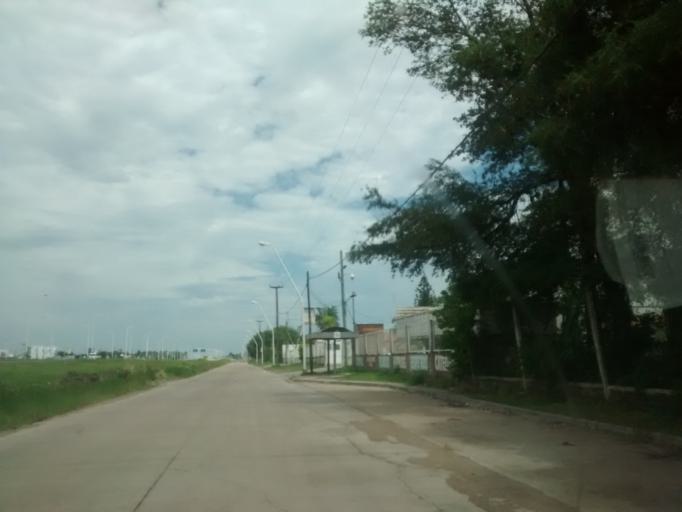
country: AR
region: Chaco
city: Resistencia
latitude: -27.4162
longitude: -58.9671
